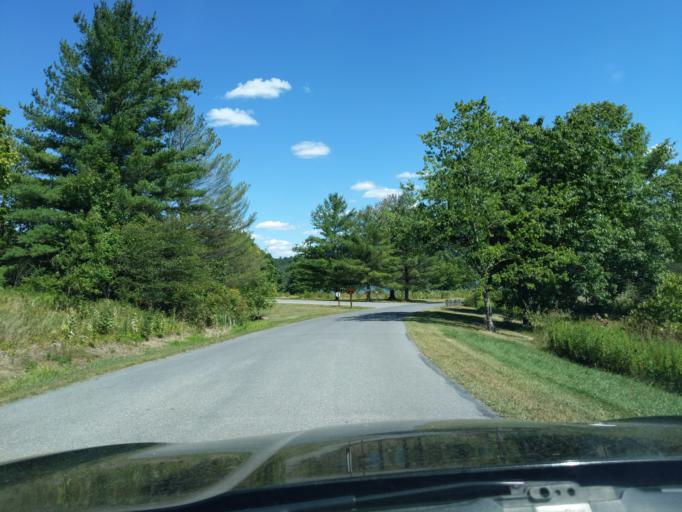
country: US
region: Pennsylvania
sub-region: Blair County
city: Greenwood
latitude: 40.4847
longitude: -78.2861
